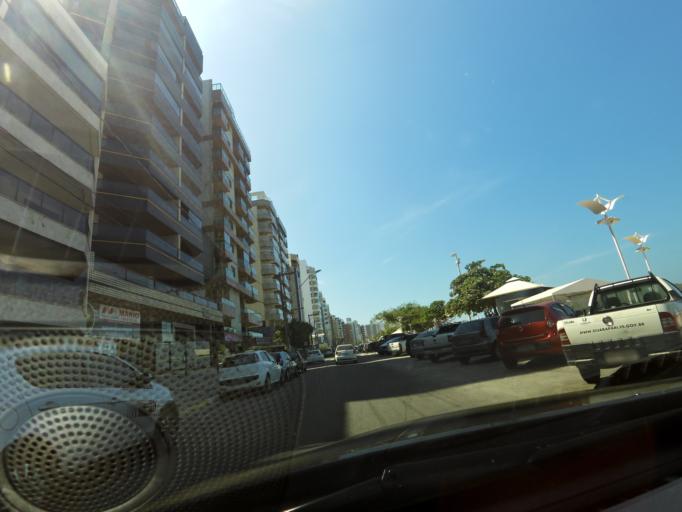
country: BR
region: Espirito Santo
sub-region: Guarapari
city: Guarapari
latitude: -20.6544
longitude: -40.4879
